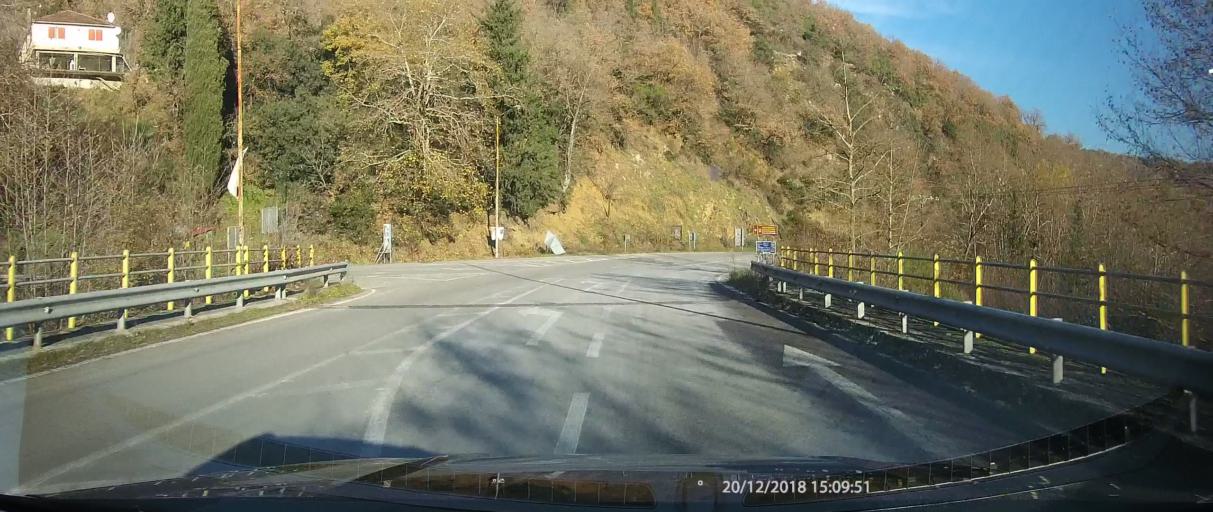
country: GR
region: Central Greece
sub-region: Nomos Evrytanias
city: Karpenisi
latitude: 38.9488
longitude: 21.9465
